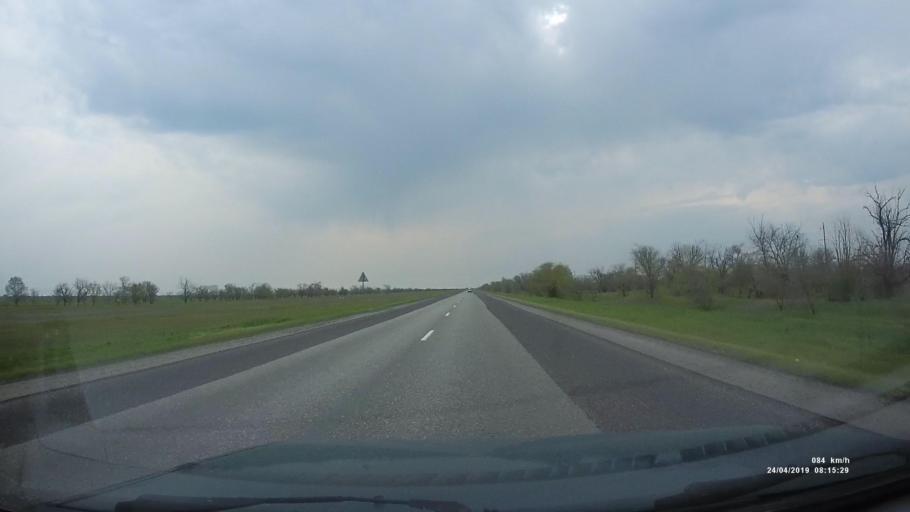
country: RU
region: Kalmykiya
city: Priyutnoye
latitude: 46.0997
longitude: 43.5945
